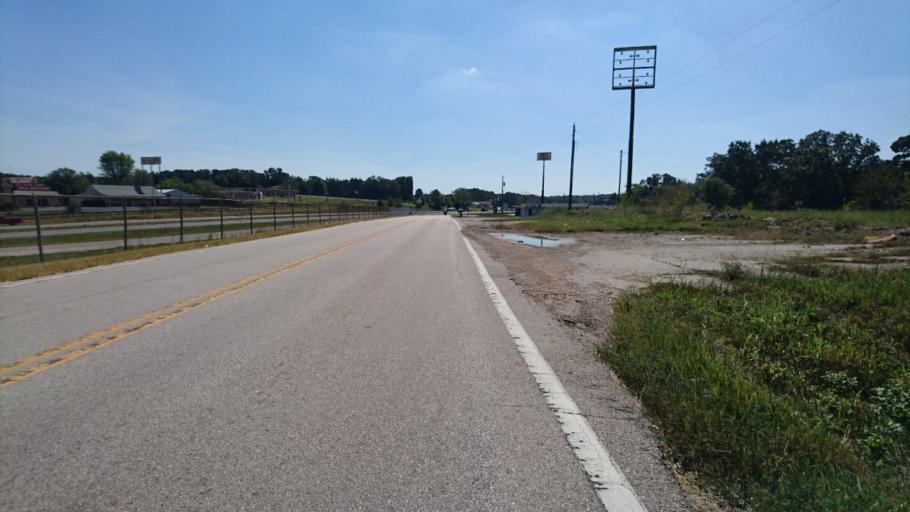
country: US
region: Missouri
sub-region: Franklin County
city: Sullivan
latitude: 38.2740
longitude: -91.1087
